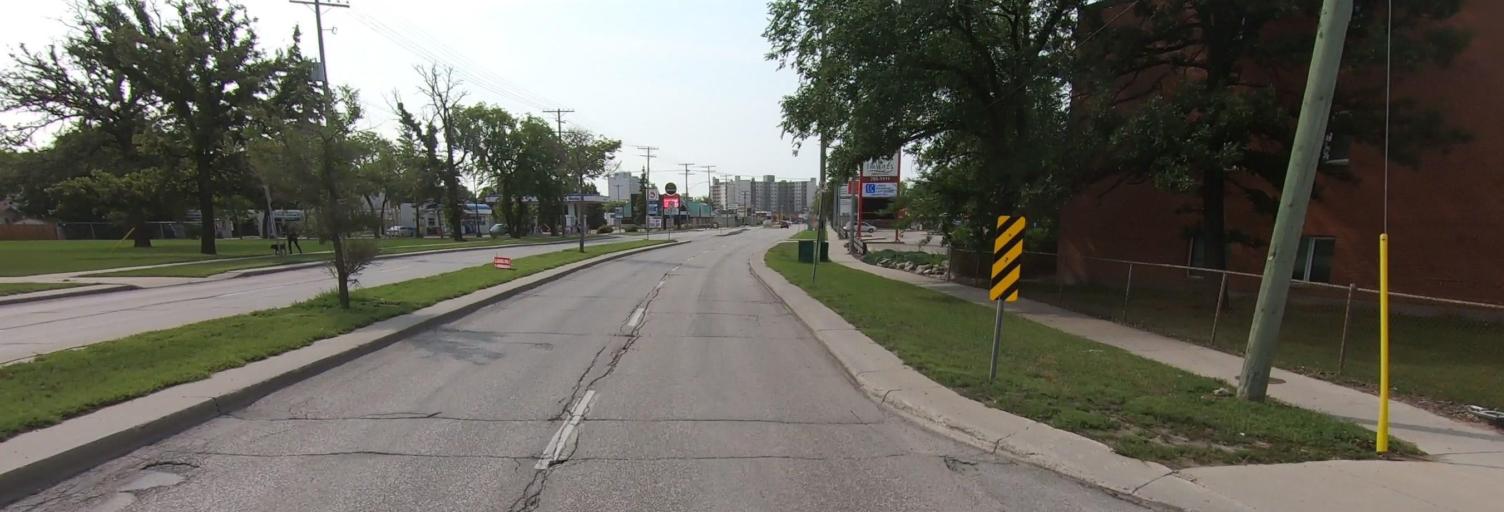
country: CA
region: Manitoba
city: Winnipeg
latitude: 49.8403
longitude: -97.1123
